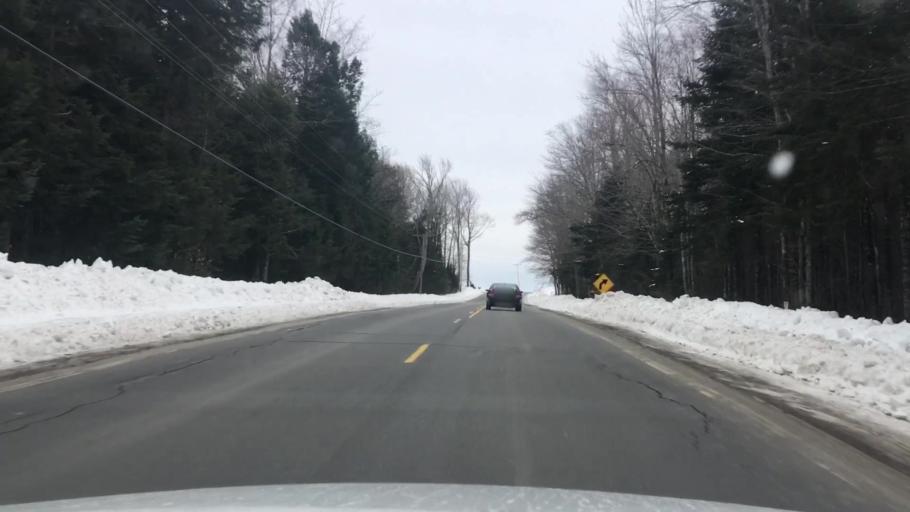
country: US
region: Maine
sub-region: Penobscot County
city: Garland
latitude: 44.9846
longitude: -69.0878
